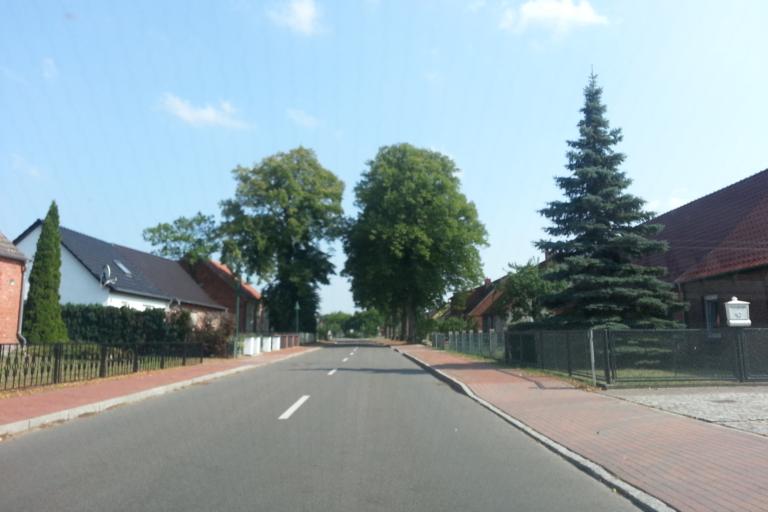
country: DE
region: Mecklenburg-Vorpommern
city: Strasburg
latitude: 53.6094
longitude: 13.7843
